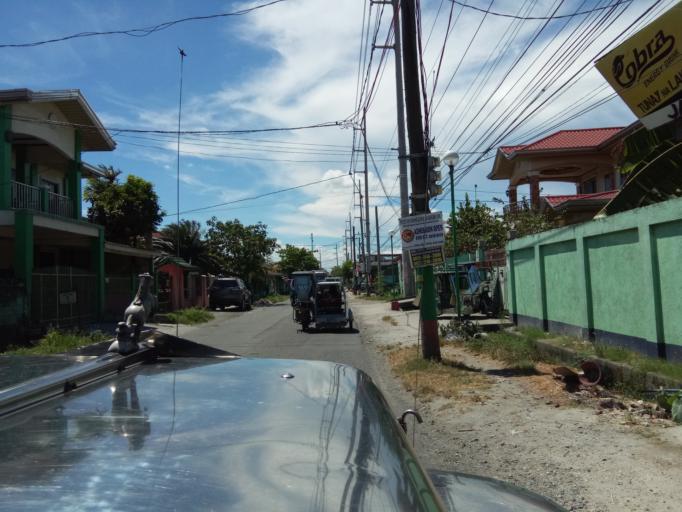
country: PH
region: Calabarzon
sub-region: Province of Cavite
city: Pasong Kawayan Primero
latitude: 14.3638
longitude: 120.8946
